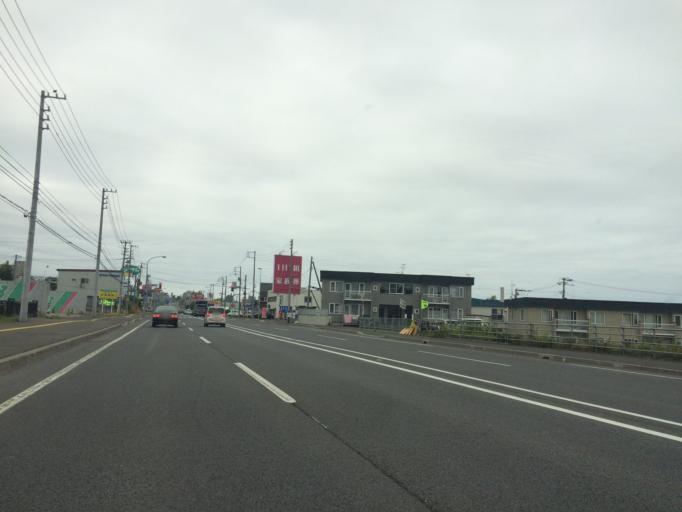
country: JP
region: Hokkaido
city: Sapporo
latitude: 43.1233
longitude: 141.2251
